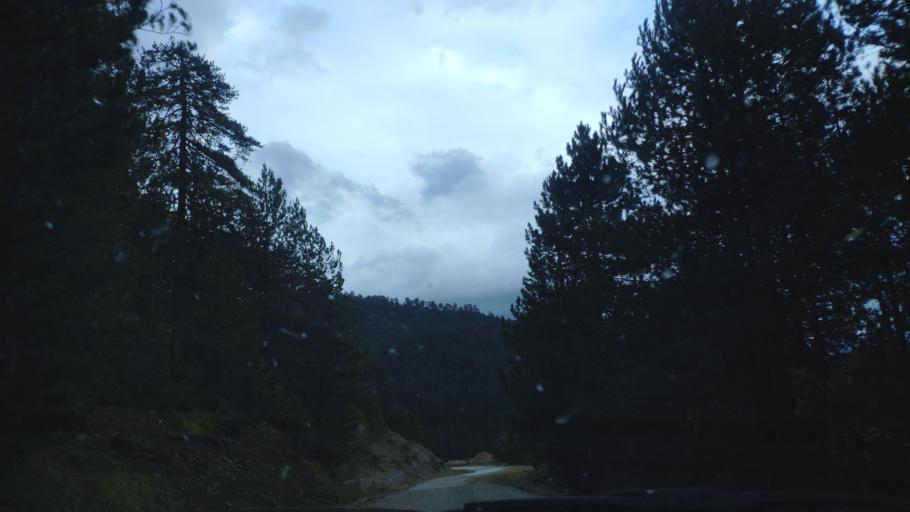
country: AL
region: Korce
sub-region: Rrethi i Kolonjes
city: Erseke
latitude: 40.2906
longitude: 20.8580
